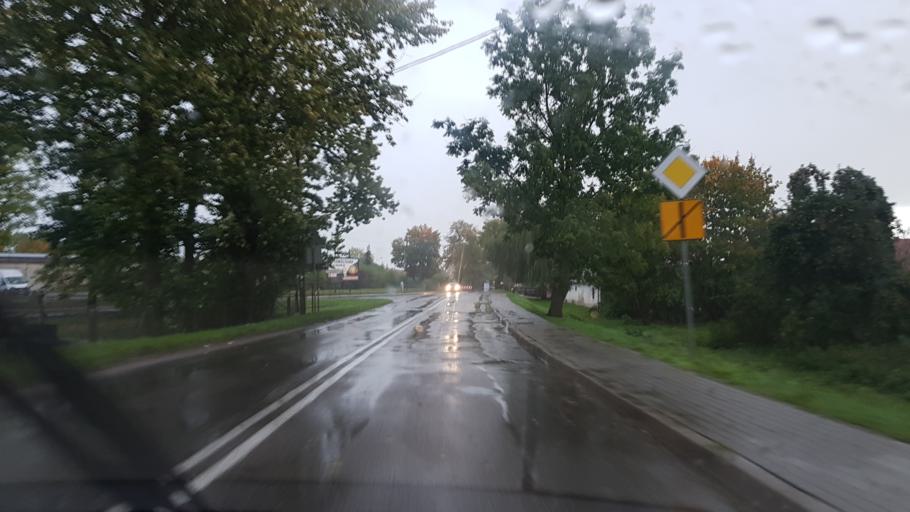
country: PL
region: Greater Poland Voivodeship
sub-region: Powiat pilski
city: Szydlowo
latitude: 53.1631
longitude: 16.6101
